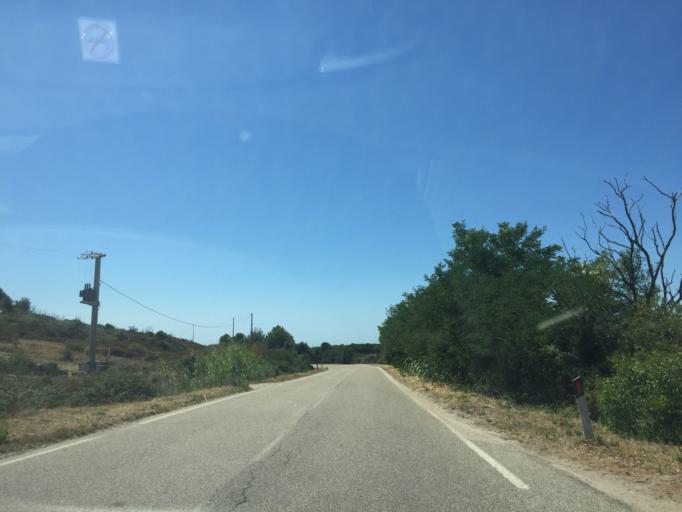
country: IT
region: Sardinia
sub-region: Provincia di Olbia-Tempio
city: Aglientu
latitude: 41.0892
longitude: 9.1165
